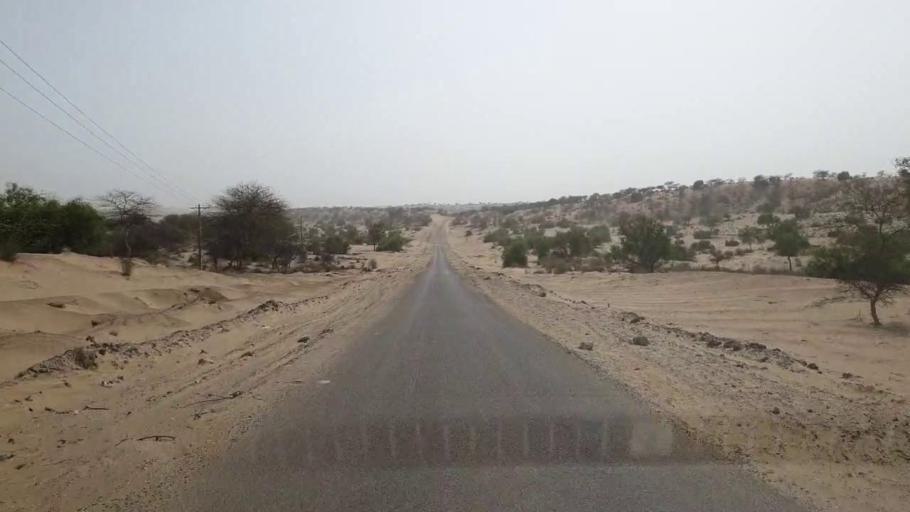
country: PK
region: Sindh
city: Mithi
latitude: 24.6201
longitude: 69.8951
